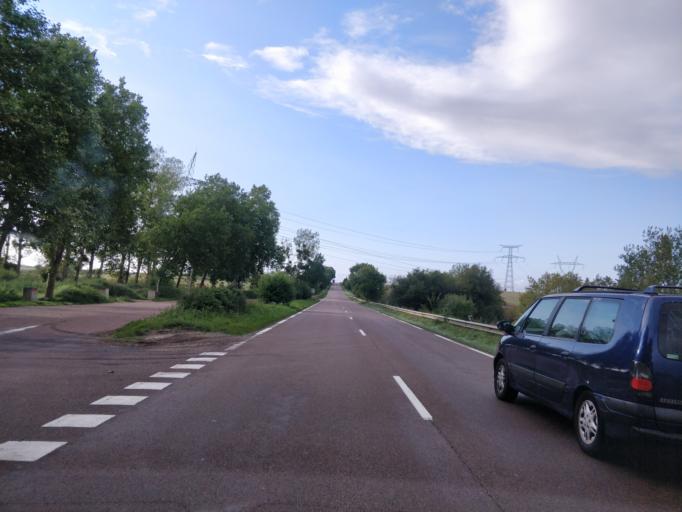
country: FR
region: Champagne-Ardenne
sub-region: Departement de l'Aube
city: Lusigny-sur-Barse
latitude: 48.2680
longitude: 4.2141
